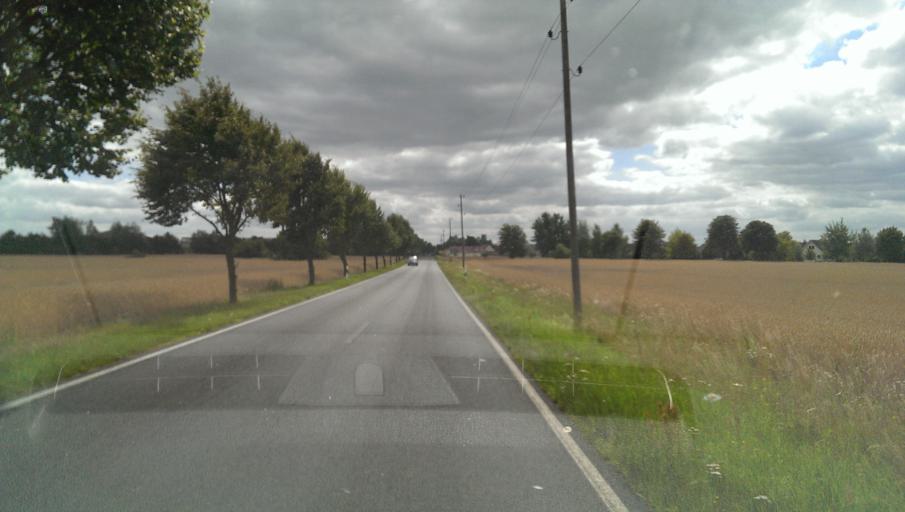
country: DE
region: Brandenburg
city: Niemegk
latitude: 52.1306
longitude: 12.7109
